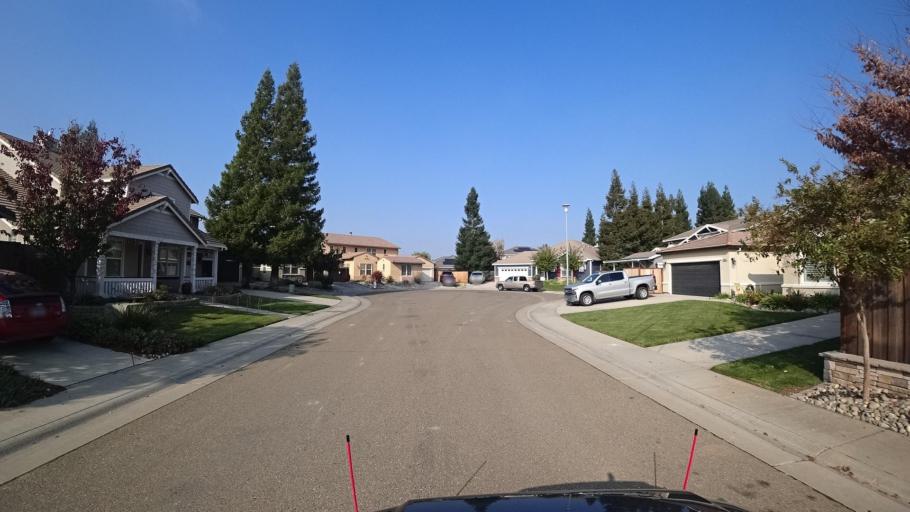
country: US
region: California
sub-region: Sacramento County
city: Elk Grove
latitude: 38.4156
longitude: -121.3388
